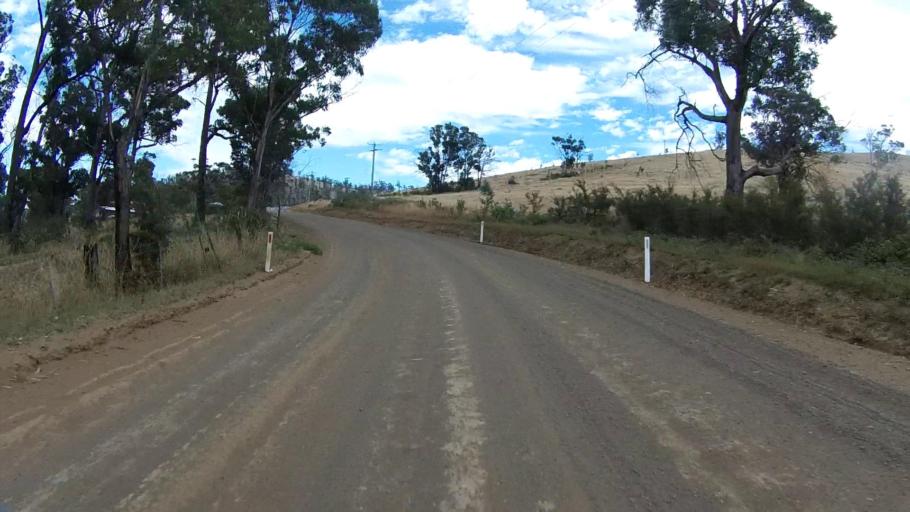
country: AU
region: Tasmania
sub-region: Sorell
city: Sorell
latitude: -42.8850
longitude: 147.7260
